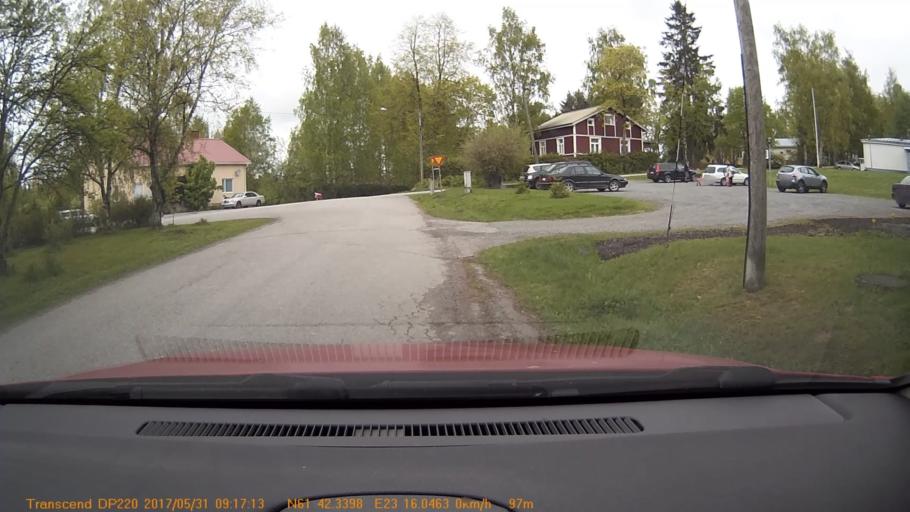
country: FI
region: Pirkanmaa
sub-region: Tampere
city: Viljakkala
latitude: 61.7057
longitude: 23.2673
